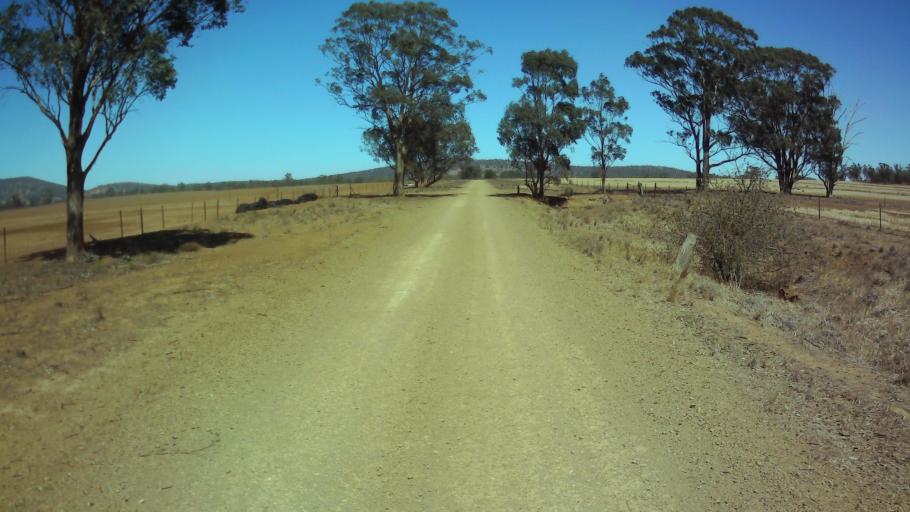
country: AU
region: New South Wales
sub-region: Weddin
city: Grenfell
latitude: -33.7070
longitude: 147.9932
